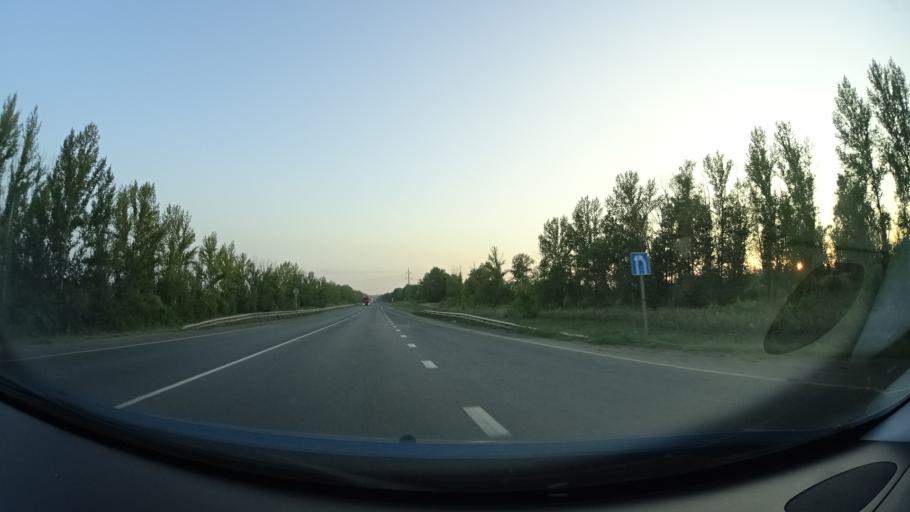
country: RU
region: Samara
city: Sukhodol
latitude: 53.8784
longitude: 51.2245
